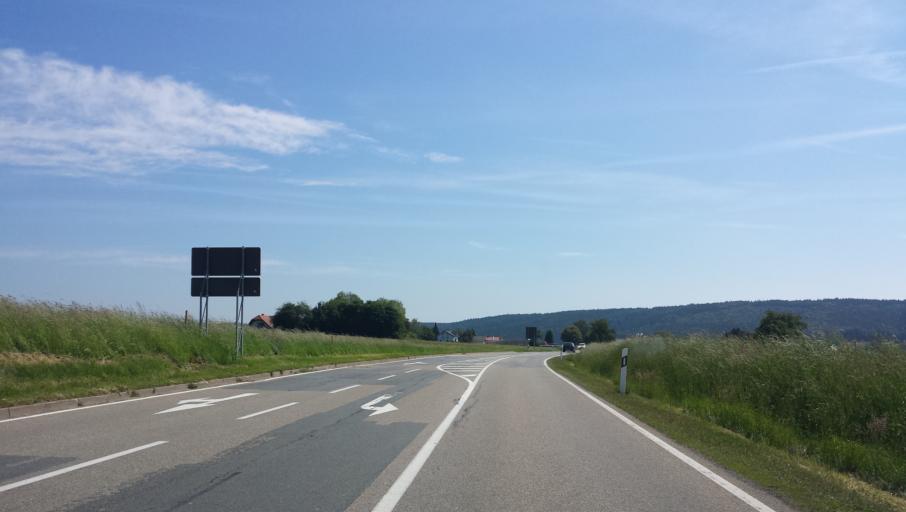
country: DE
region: Hesse
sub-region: Regierungsbezirk Darmstadt
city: Beerfelden
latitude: 49.5593
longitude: 8.9604
